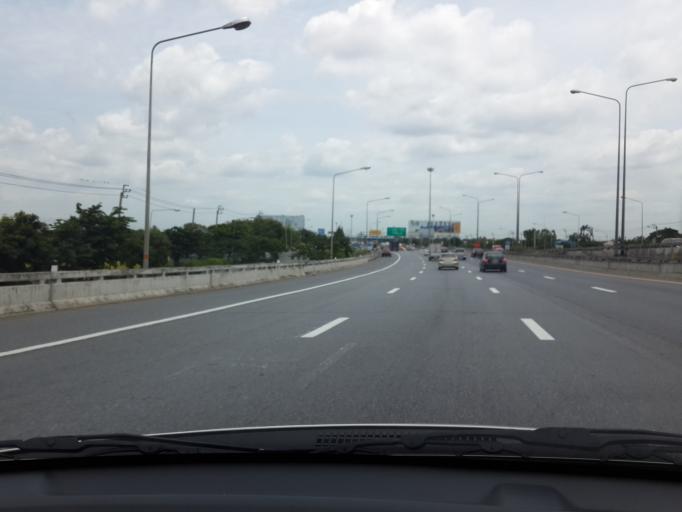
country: TH
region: Bangkok
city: Saphan Sung
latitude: 13.7496
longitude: 100.7022
